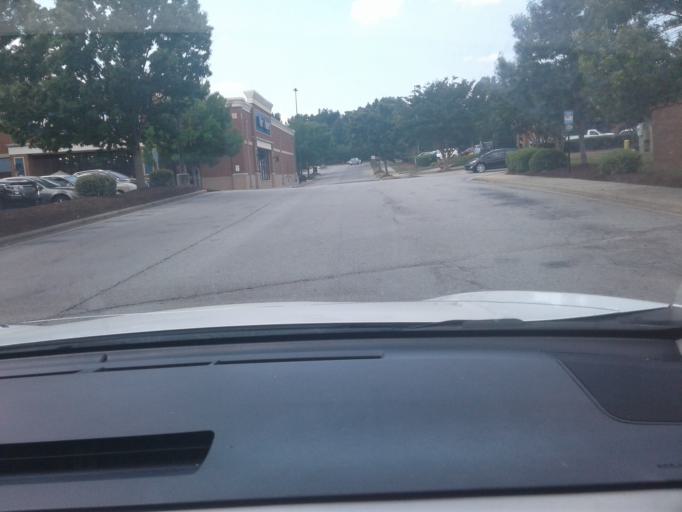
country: US
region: North Carolina
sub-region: Wake County
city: Garner
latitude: 35.6922
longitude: -78.5814
